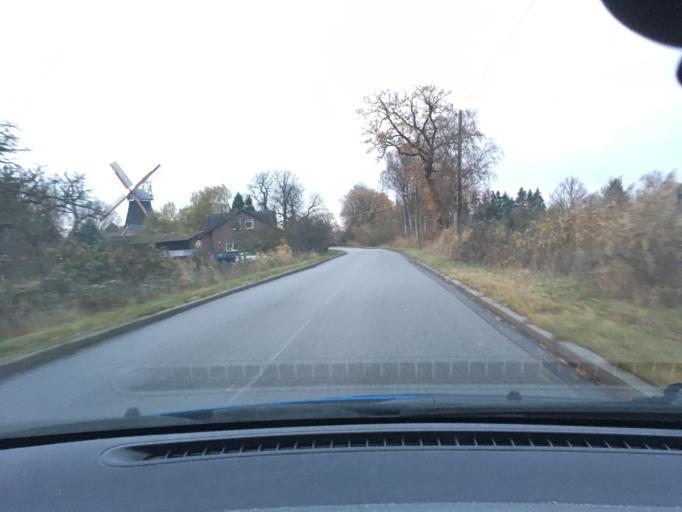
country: DE
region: Lower Saxony
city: Winsen
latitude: 53.4098
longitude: 10.2092
